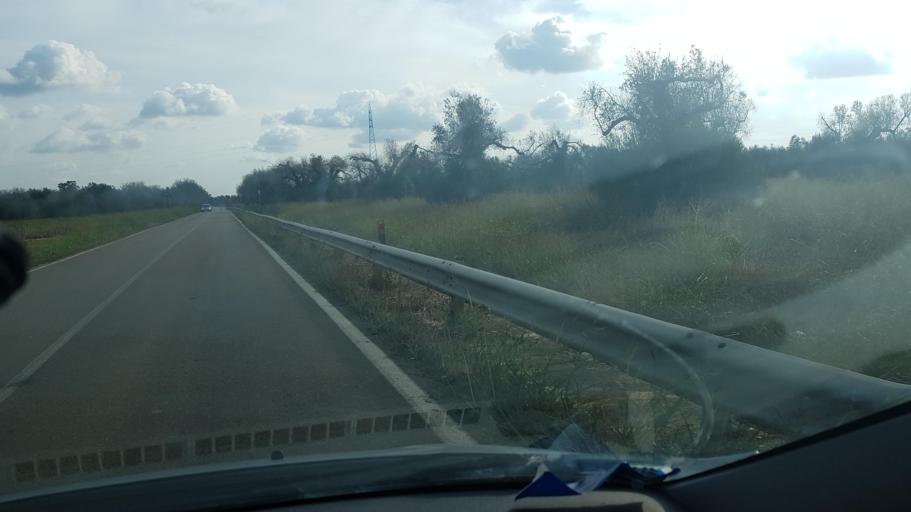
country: IT
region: Apulia
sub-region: Provincia di Brindisi
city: Cellino San Marco
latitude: 40.4493
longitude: 17.9548
